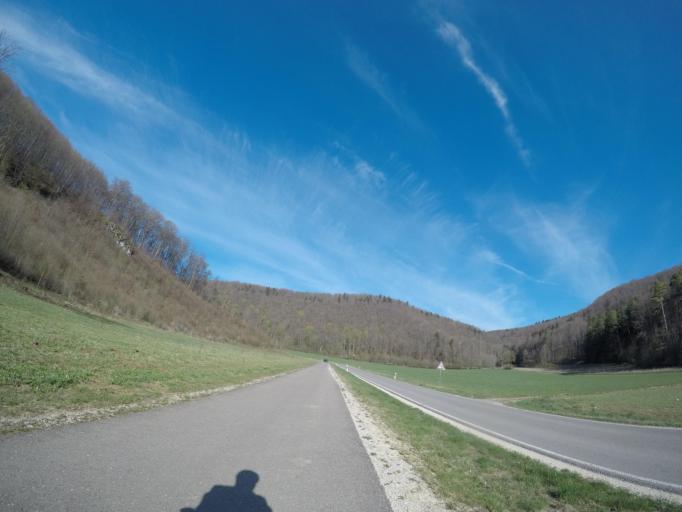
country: DE
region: Baden-Wuerttemberg
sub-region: Tuebingen Region
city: Allmendingen
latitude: 48.3477
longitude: 9.7051
